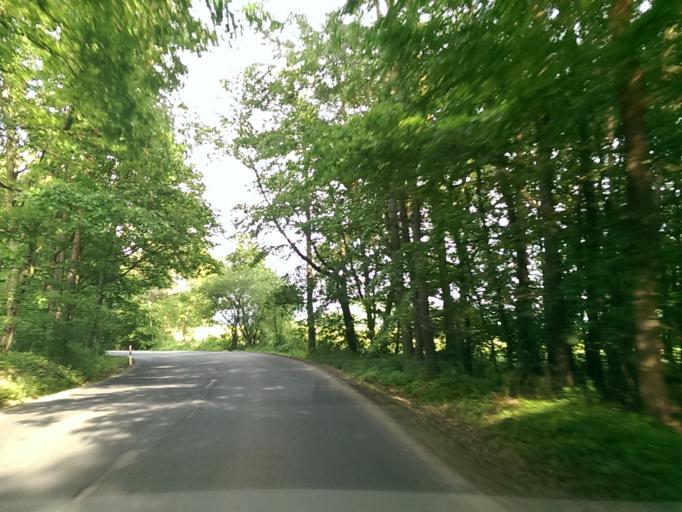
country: CZ
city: Duba
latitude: 50.5546
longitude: 14.5933
